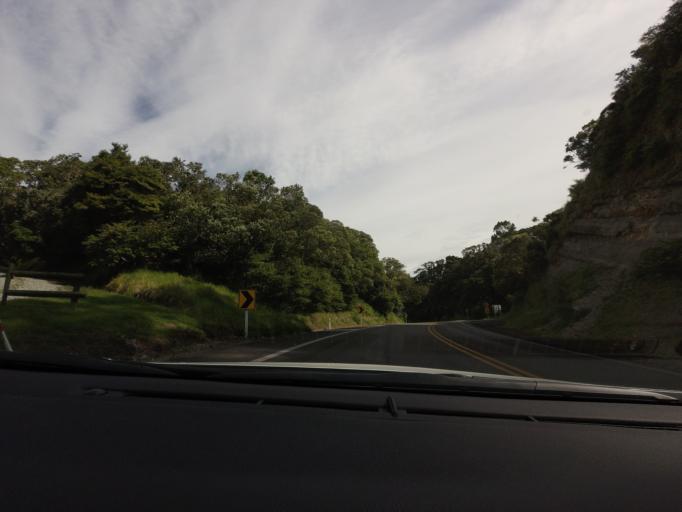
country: NZ
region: Auckland
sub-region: Auckland
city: Warkworth
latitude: -36.5495
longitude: 174.7063
